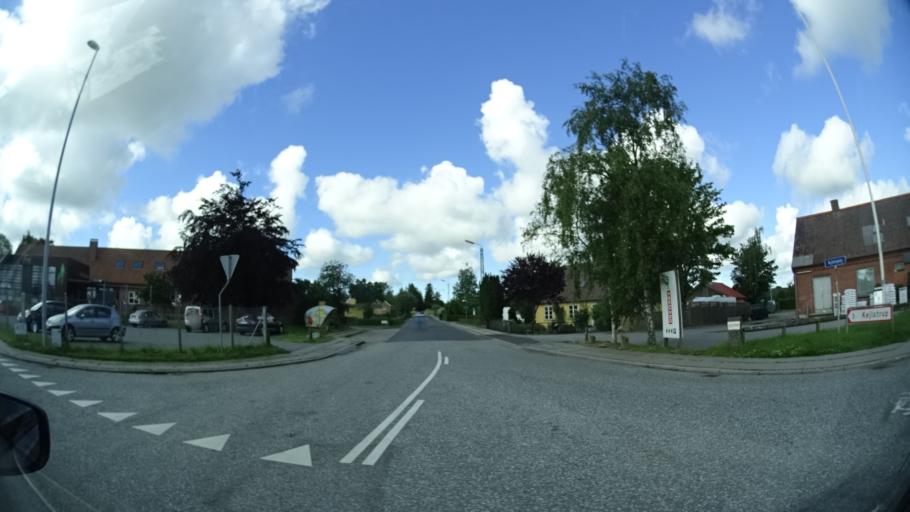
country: DK
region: Central Jutland
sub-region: Syddjurs Kommune
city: Ronde
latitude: 56.2847
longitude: 10.5853
